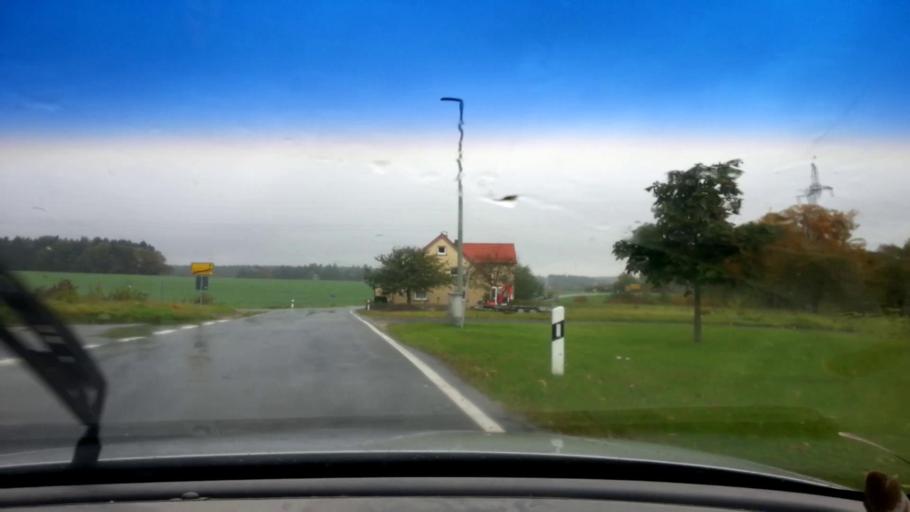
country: DE
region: Bavaria
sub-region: Upper Franconia
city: Stadelhofen
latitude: 50.0052
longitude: 11.1992
